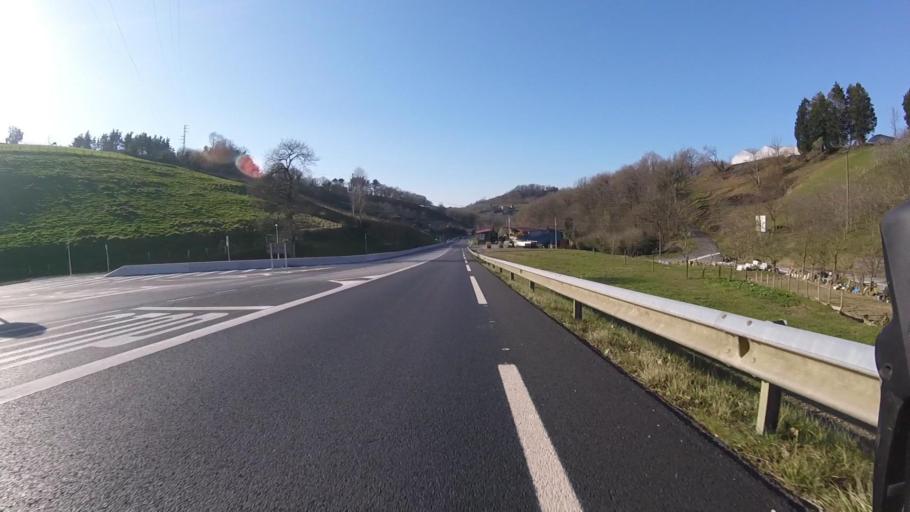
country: ES
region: Basque Country
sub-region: Provincia de Guipuzcoa
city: Astigarraga
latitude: 43.2837
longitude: -1.9283
